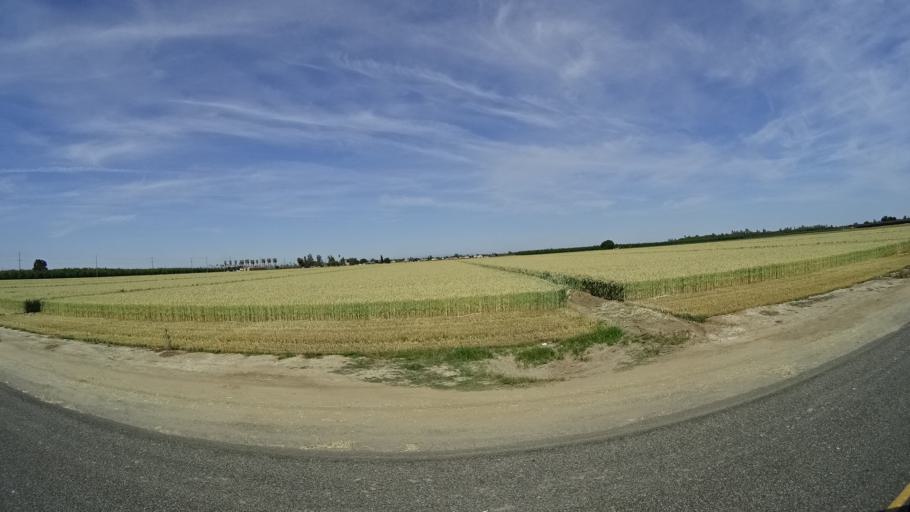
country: US
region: California
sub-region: Kings County
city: Hanford
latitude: 36.3446
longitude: -119.6100
